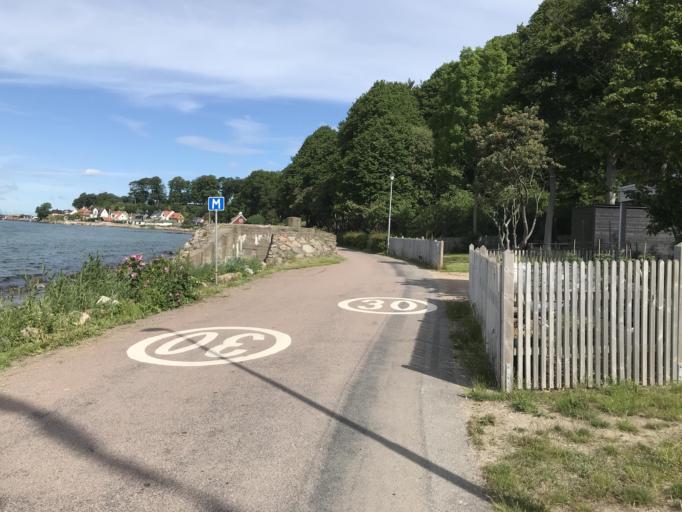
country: SE
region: Skane
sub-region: Helsingborg
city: Rydeback
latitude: 55.9368
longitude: 12.7828
